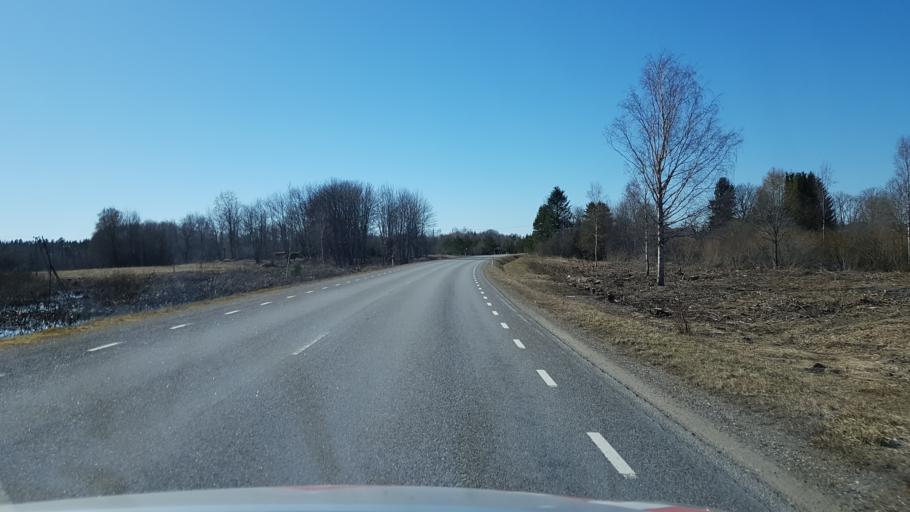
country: EE
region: Ida-Virumaa
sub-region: Aseri vald
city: Aseri
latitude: 59.3478
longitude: 26.7665
